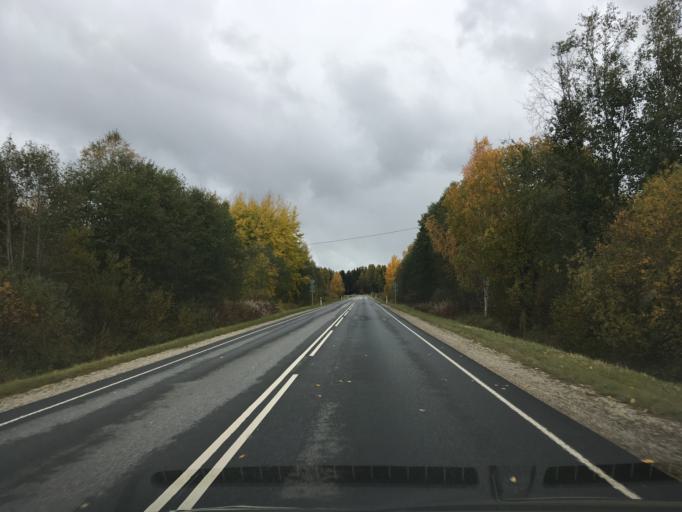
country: EE
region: Harju
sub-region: Anija vald
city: Kehra
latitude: 59.3142
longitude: 25.3436
